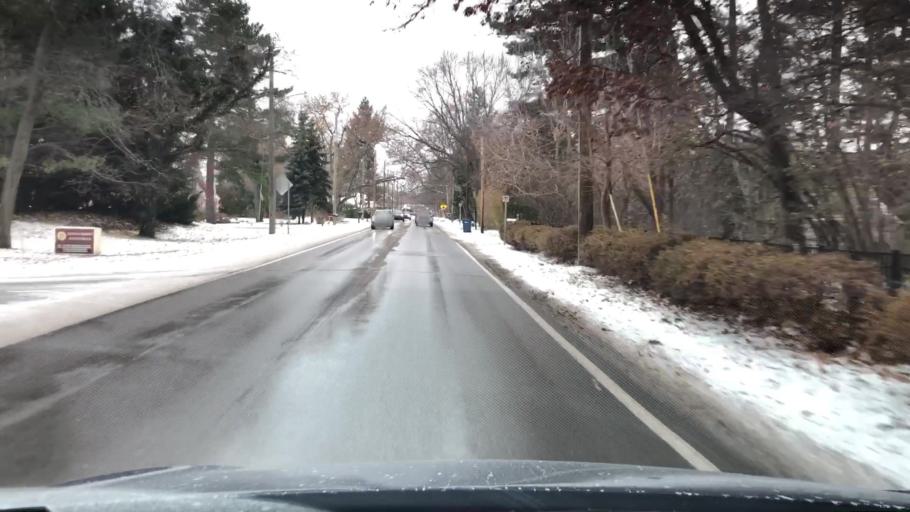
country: US
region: Michigan
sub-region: Grand Traverse County
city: Traverse City
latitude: 44.7657
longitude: -85.5966
